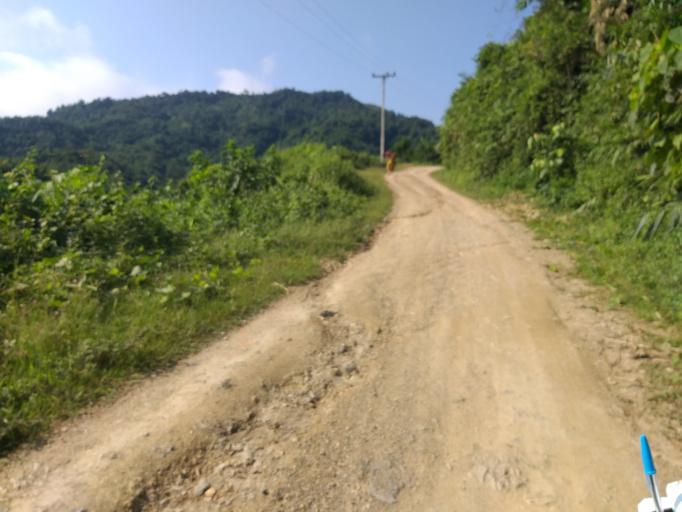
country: LA
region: Phongsali
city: Khoa
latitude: 21.2011
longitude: 102.6833
